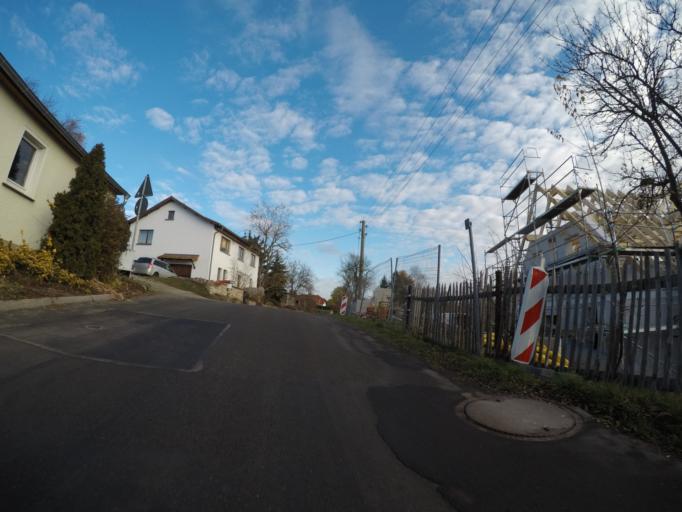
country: DE
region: Thuringia
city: Vollmershain
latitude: 50.8506
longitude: 12.3024
